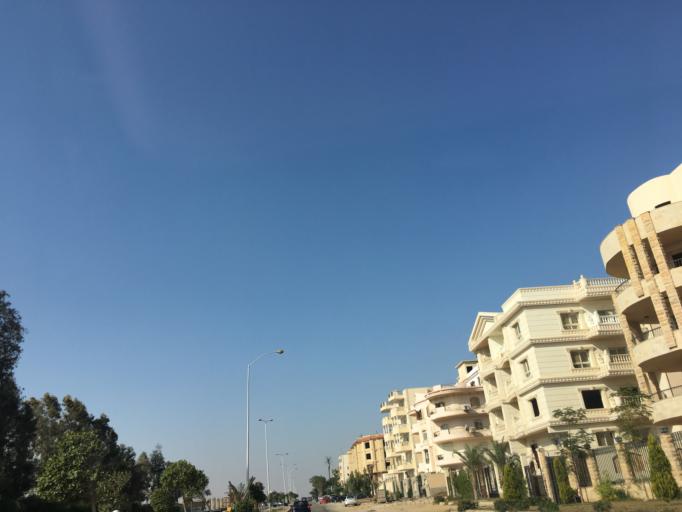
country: EG
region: Al Jizah
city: Madinat Sittah Uktubar
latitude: 29.9983
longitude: 30.9761
